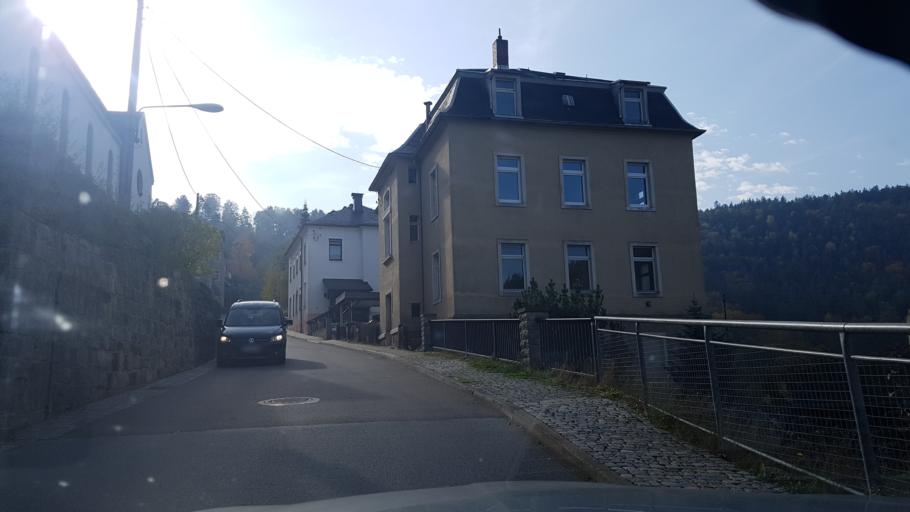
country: DE
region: Saxony
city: Konigstein
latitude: 50.9149
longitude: 14.0720
